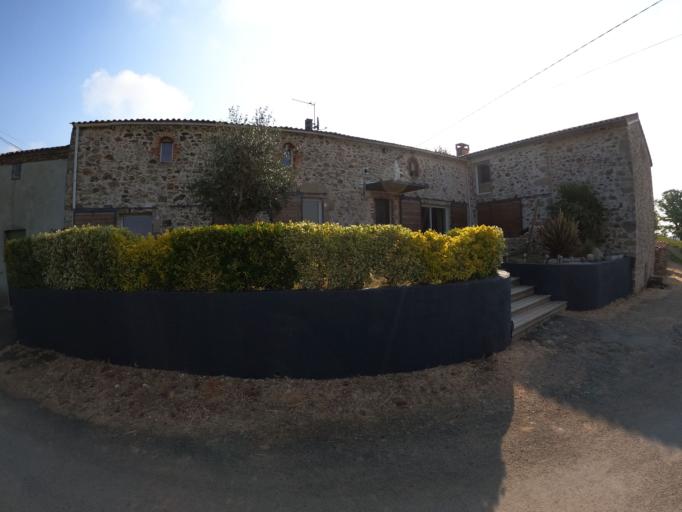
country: FR
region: Pays de la Loire
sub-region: Departement de Maine-et-Loire
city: La Romagne
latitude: 47.0709
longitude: -1.0054
